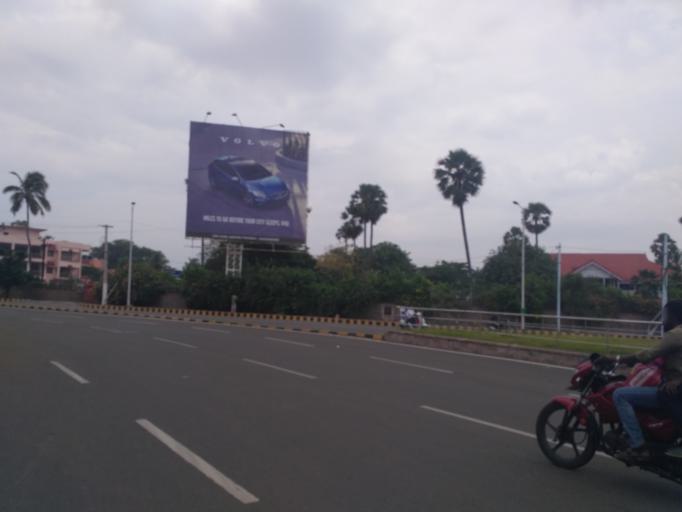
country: IN
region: Andhra Pradesh
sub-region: Vishakhapatnam
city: Yarada
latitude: 17.7217
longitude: 83.3353
